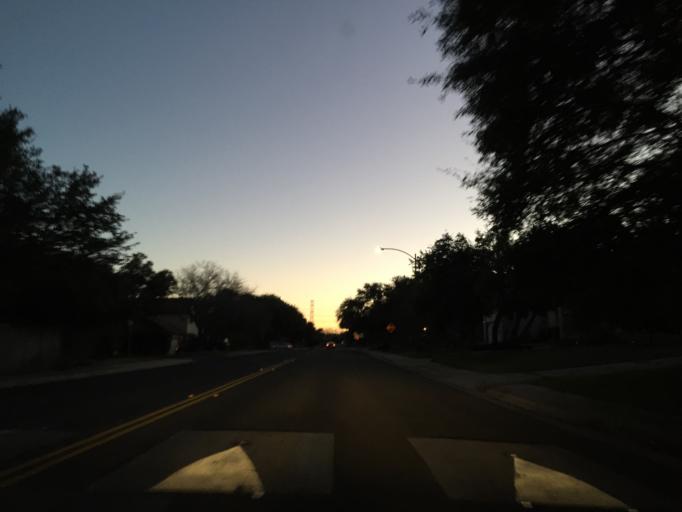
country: US
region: Texas
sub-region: Travis County
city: Wells Branch
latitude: 30.3975
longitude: -97.6952
